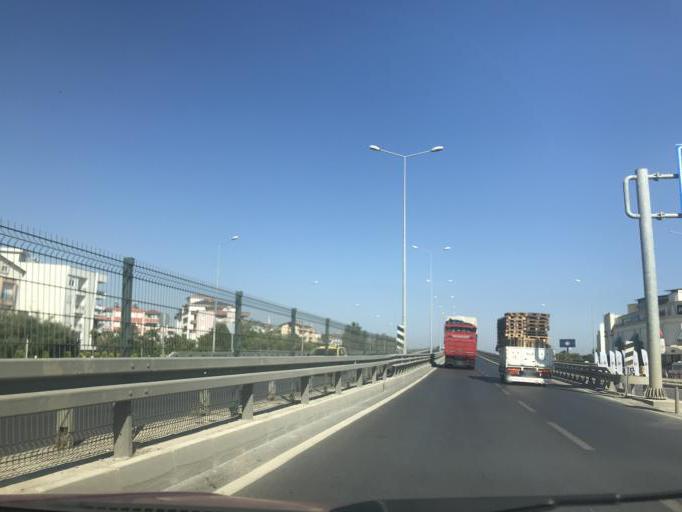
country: TR
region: Antalya
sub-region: Manavgat
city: Manavgat
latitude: 36.7824
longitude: 31.4247
